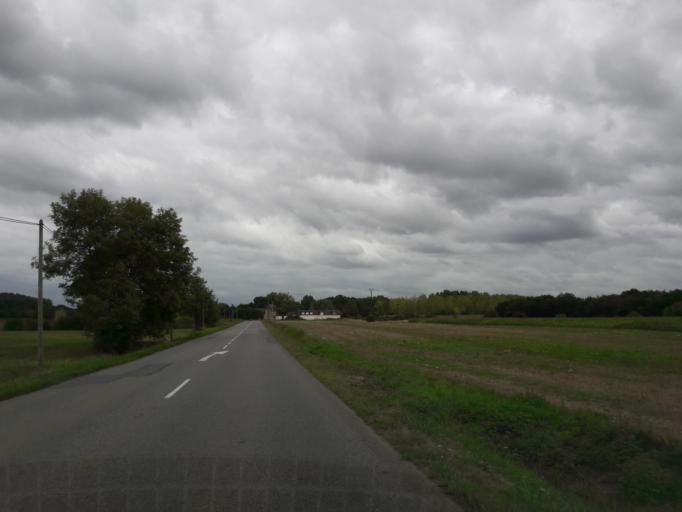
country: FR
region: Brittany
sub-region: Departement d'Ille-et-Vilaine
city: Chartres-de-Bretagne
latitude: 48.0212
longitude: -1.7205
